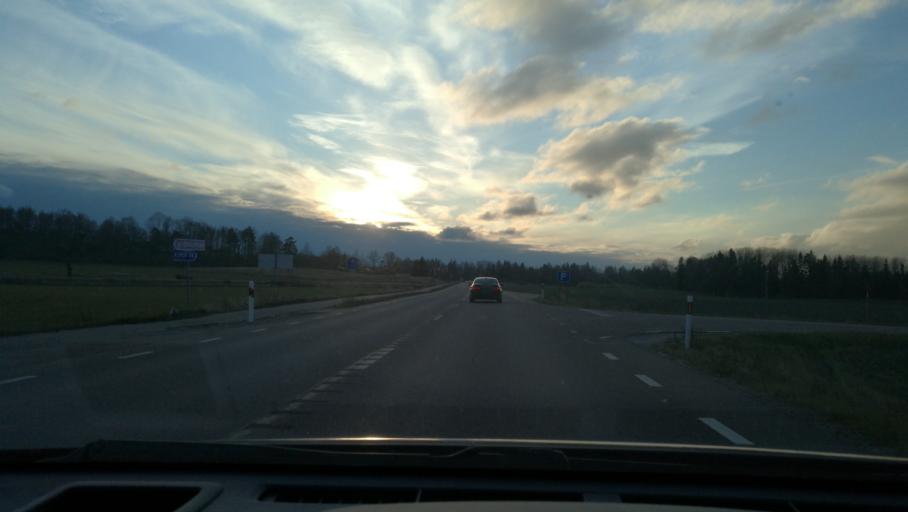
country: SE
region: Soedermanland
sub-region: Katrineholms Kommun
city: Katrineholm
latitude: 59.1526
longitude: 16.0759
